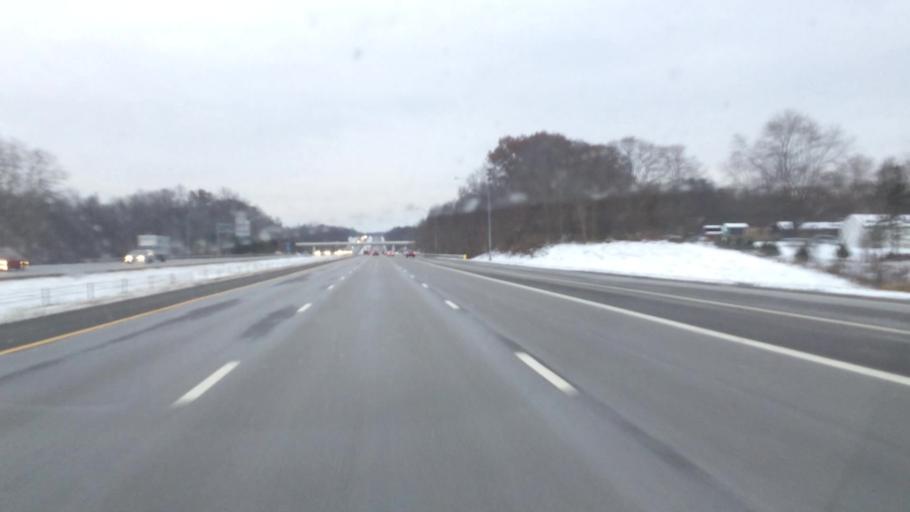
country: US
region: Ohio
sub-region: Medina County
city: Brunswick
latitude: 41.1903
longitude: -81.7903
